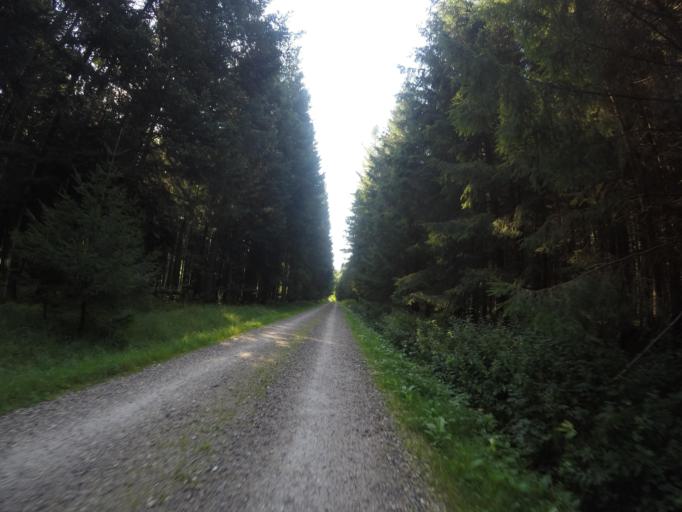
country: DE
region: Baden-Wuerttemberg
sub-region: Tuebingen Region
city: Schnurpflingen
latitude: 48.2502
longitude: 10.0079
